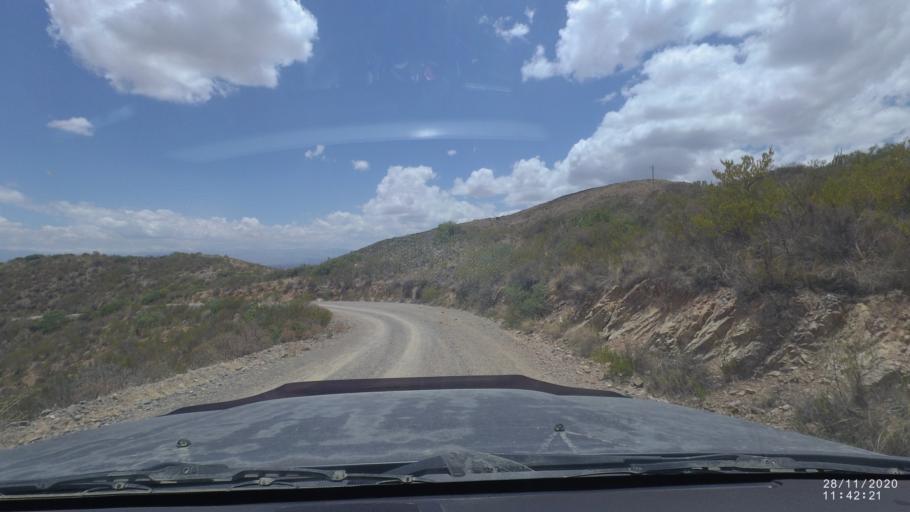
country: BO
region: Cochabamba
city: Tarata
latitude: -17.6651
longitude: -66.0474
